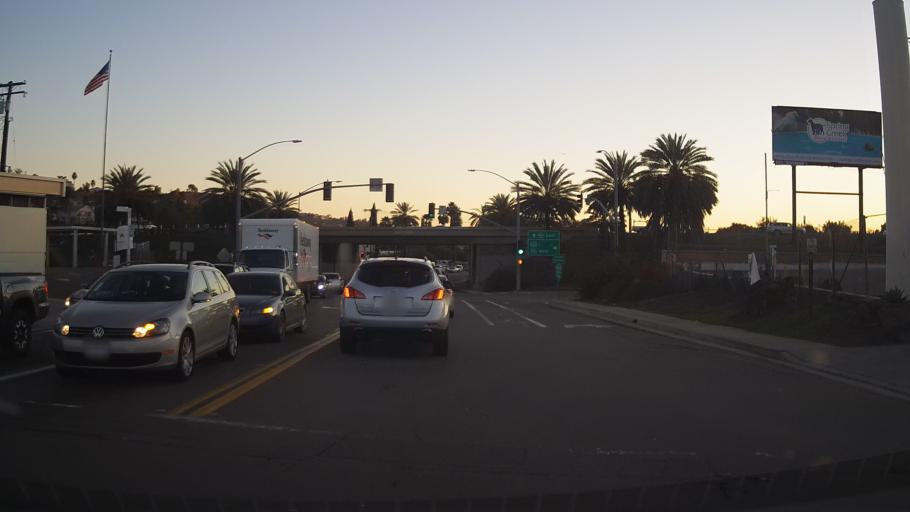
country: US
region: California
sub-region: San Diego County
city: Spring Valley
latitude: 32.7514
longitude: -117.0015
